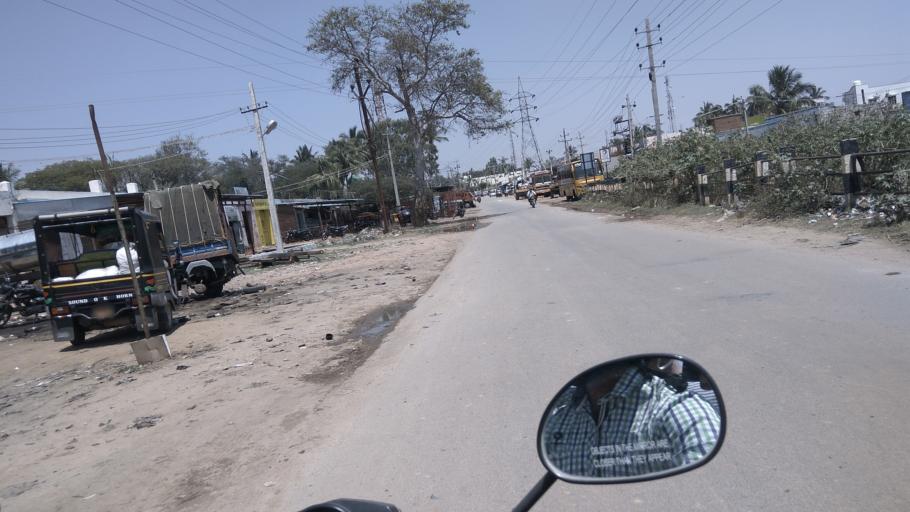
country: IN
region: Karnataka
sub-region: Kolar
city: Mulbagal
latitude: 13.1558
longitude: 78.3906
